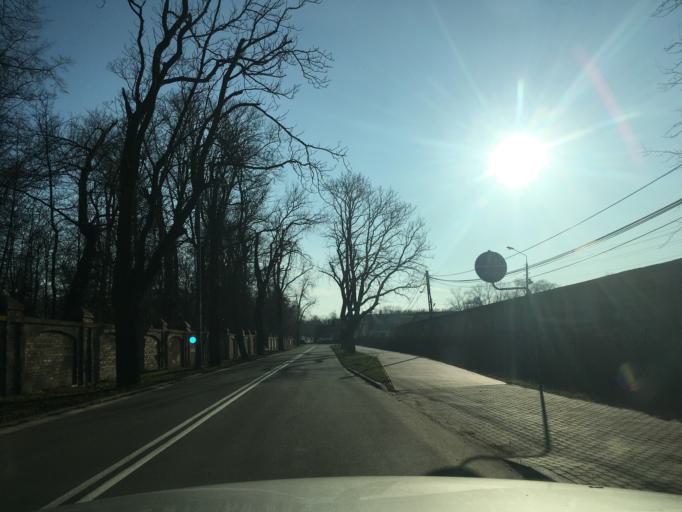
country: PL
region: Masovian Voivodeship
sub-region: Powiat pruszkowski
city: Nadarzyn
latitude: 52.0496
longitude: 20.7824
